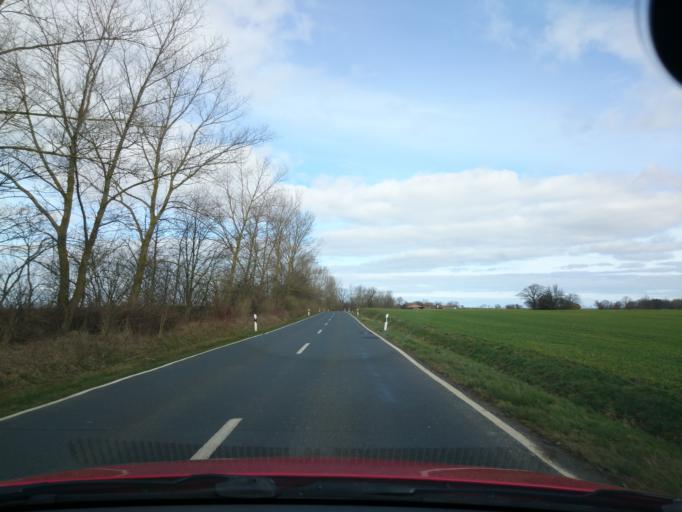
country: DE
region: Mecklenburg-Vorpommern
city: Velgast
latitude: 54.3171
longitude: 12.7928
